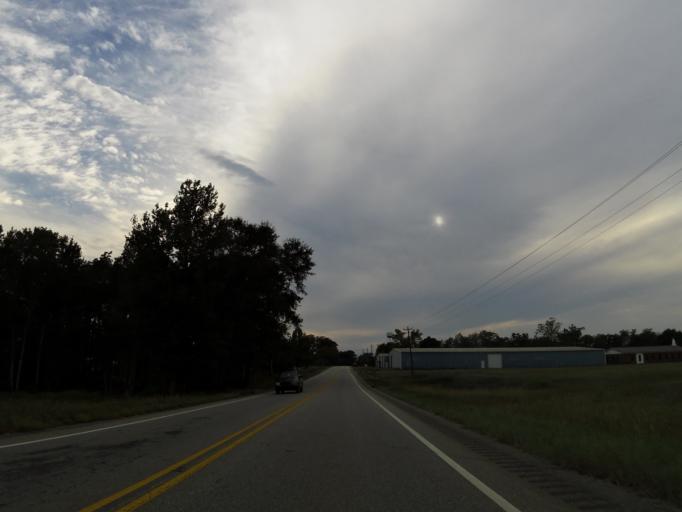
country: US
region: Alabama
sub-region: Monroe County
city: Frisco City
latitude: 31.3085
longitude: -87.4924
